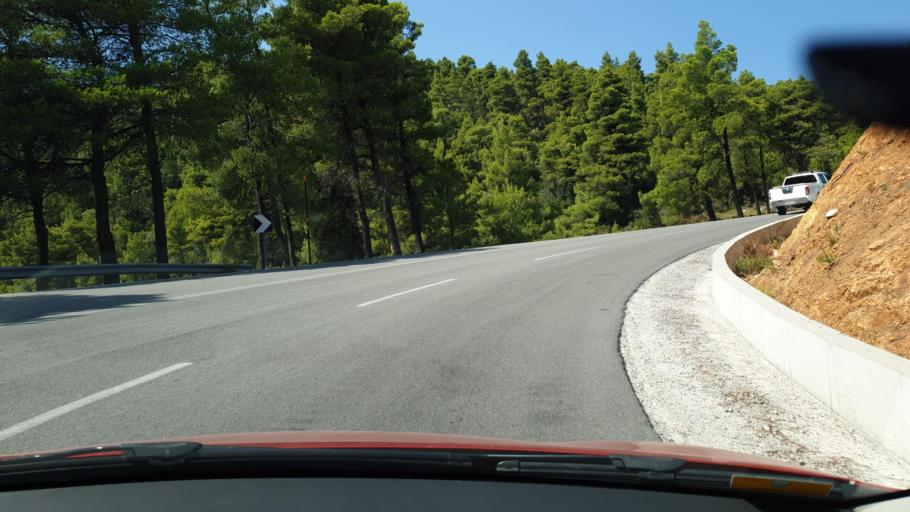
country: GR
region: Central Greece
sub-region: Nomos Evvoias
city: Politika
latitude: 38.6357
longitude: 23.5653
